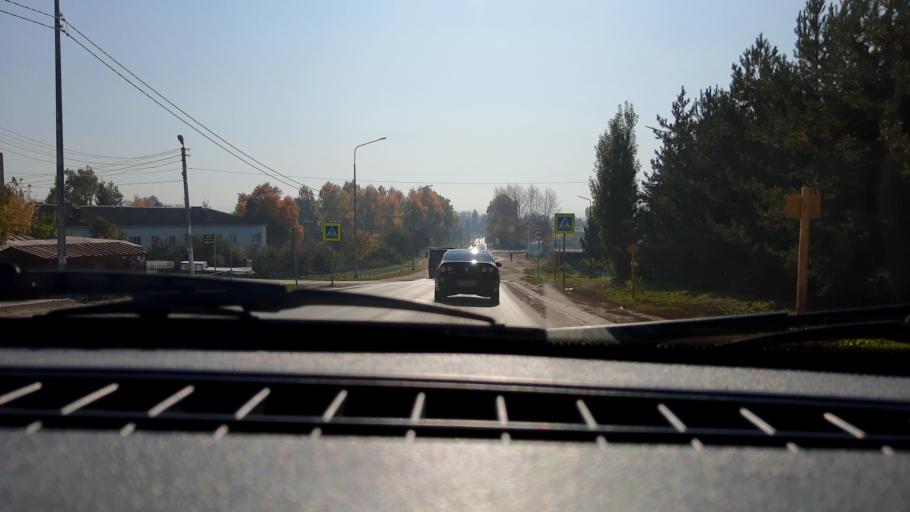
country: RU
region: Bashkortostan
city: Mikhaylovka
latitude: 54.8076
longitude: 55.8892
